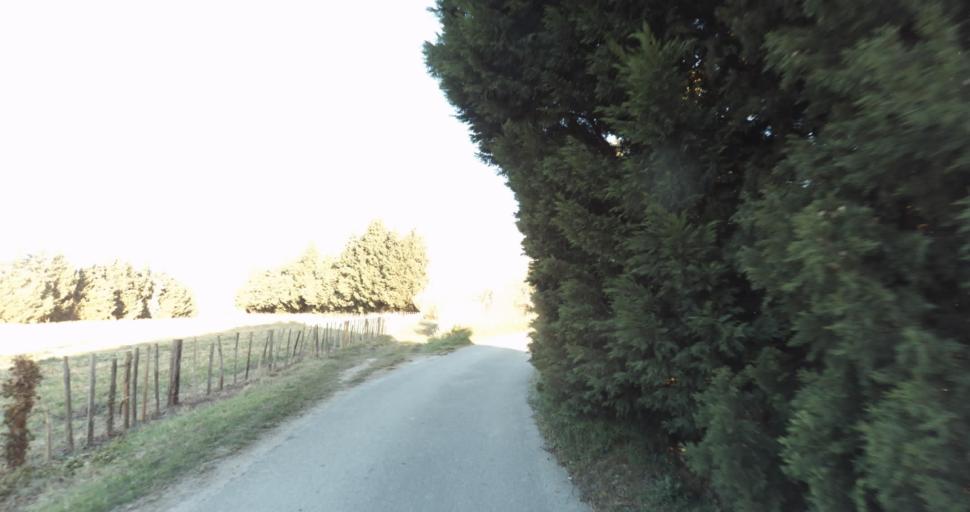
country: FR
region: Provence-Alpes-Cote d'Azur
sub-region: Departement des Bouches-du-Rhone
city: Barbentane
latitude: 43.9146
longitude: 4.7703
